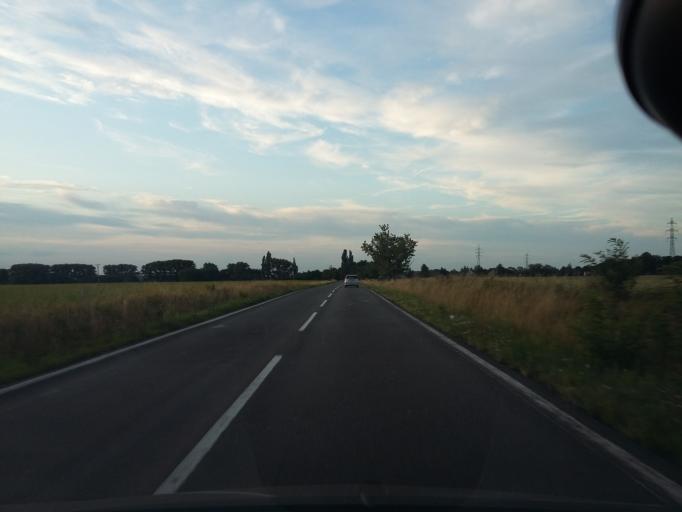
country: SK
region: Bratislavsky
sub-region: Okres Malacky
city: Malacky
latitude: 48.4259
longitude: 17.1602
